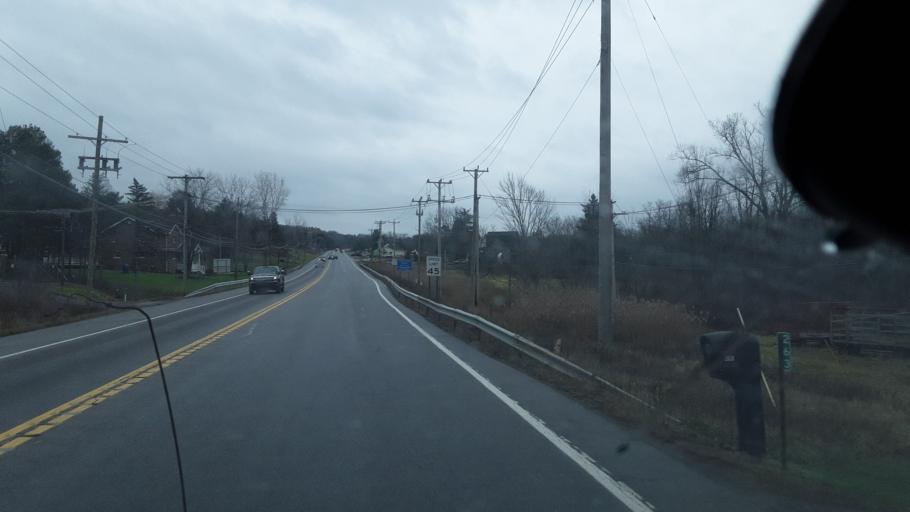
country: US
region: New York
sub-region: Erie County
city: Holland
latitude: 42.6363
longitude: -78.5340
